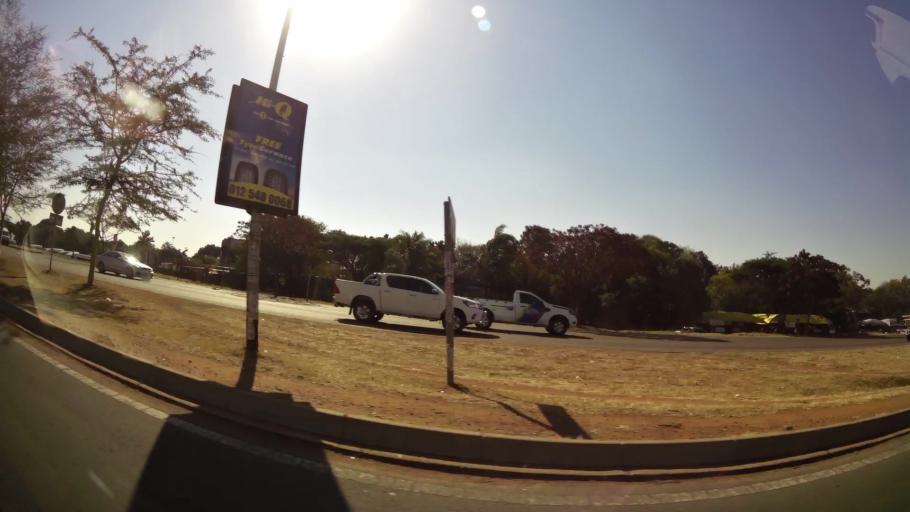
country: ZA
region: Gauteng
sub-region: City of Tshwane Metropolitan Municipality
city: Pretoria
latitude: -25.6791
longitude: 28.2495
